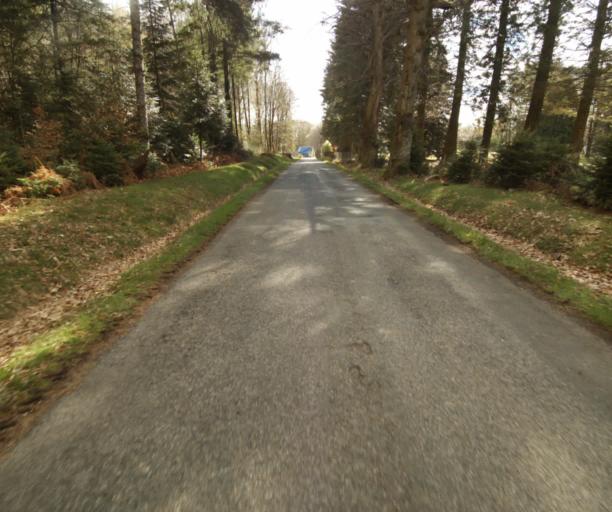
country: FR
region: Limousin
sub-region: Departement de la Correze
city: Correze
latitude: 45.2475
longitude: 1.9414
